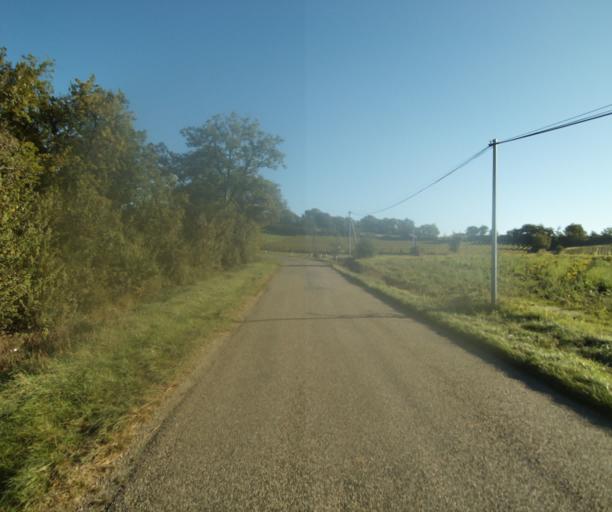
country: FR
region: Midi-Pyrenees
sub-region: Departement du Gers
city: Gondrin
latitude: 43.8505
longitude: 0.2479
